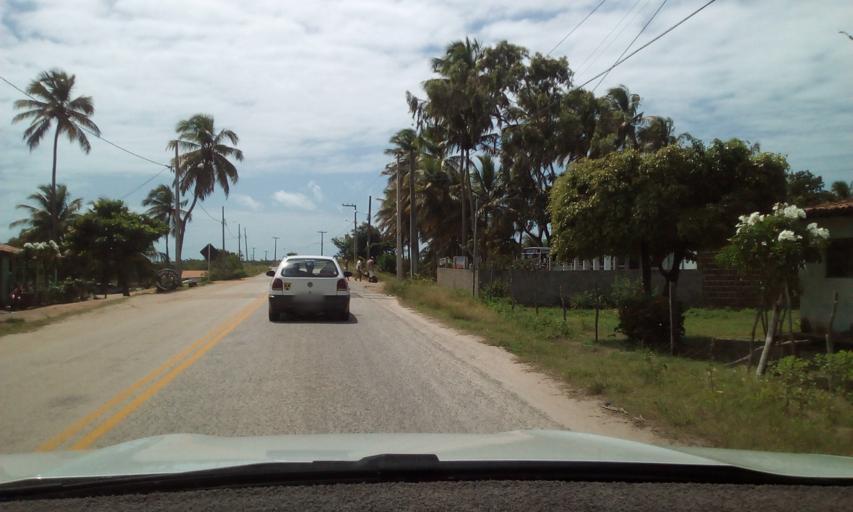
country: BR
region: Paraiba
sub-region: Rio Tinto
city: Rio Tinto
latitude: -6.7163
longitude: -34.9448
